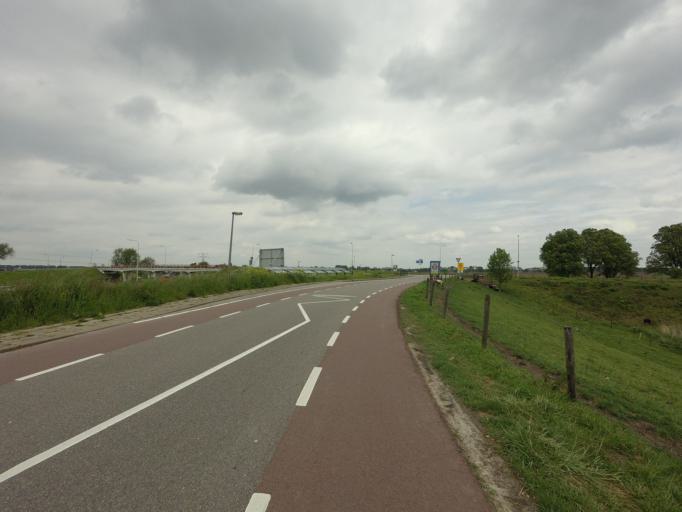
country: NL
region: North Brabant
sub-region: Gemeente Moerdijk
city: Willemstad
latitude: 51.7321
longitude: 4.4112
